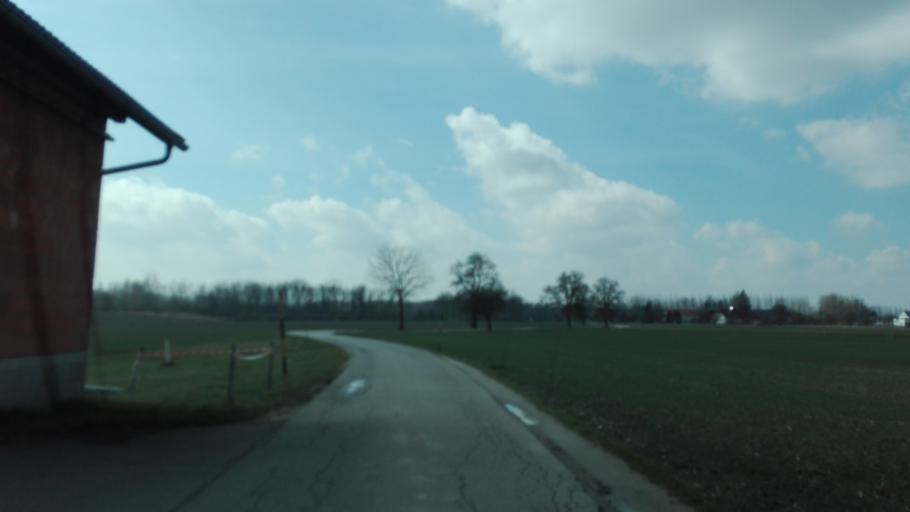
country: AT
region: Upper Austria
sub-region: Politischer Bezirk Urfahr-Umgebung
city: Ottensheim
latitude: 48.3256
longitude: 14.1481
